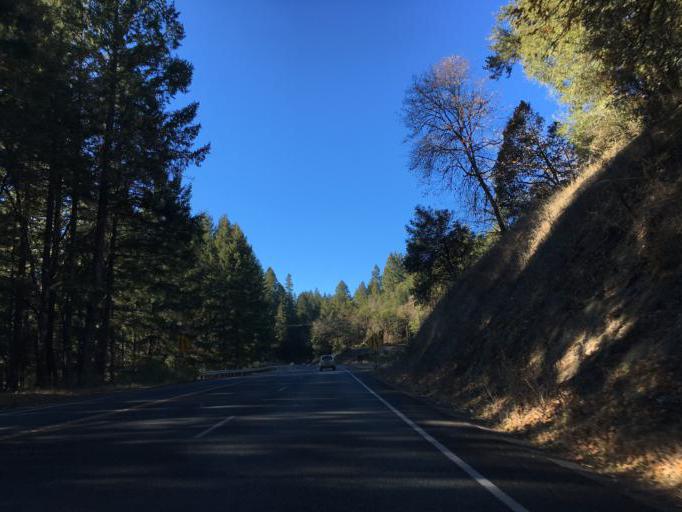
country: US
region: California
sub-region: Mendocino County
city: Brooktrails
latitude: 39.4699
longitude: -123.3582
